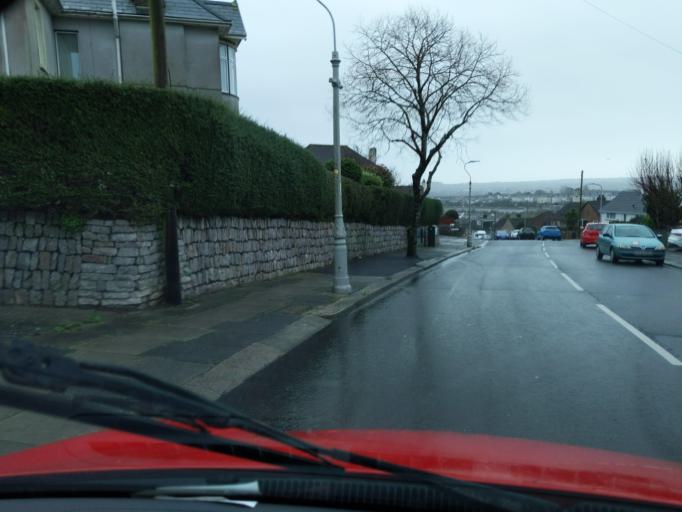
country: GB
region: England
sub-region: Plymouth
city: Plymouth
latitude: 50.3850
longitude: -4.1245
